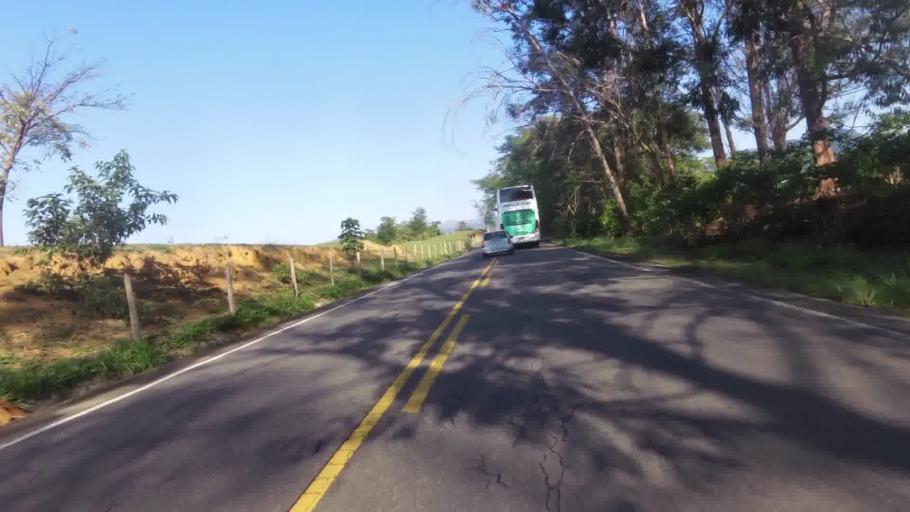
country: BR
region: Espirito Santo
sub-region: Alfredo Chaves
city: Alfredo Chaves
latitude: -20.6665
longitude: -40.7212
